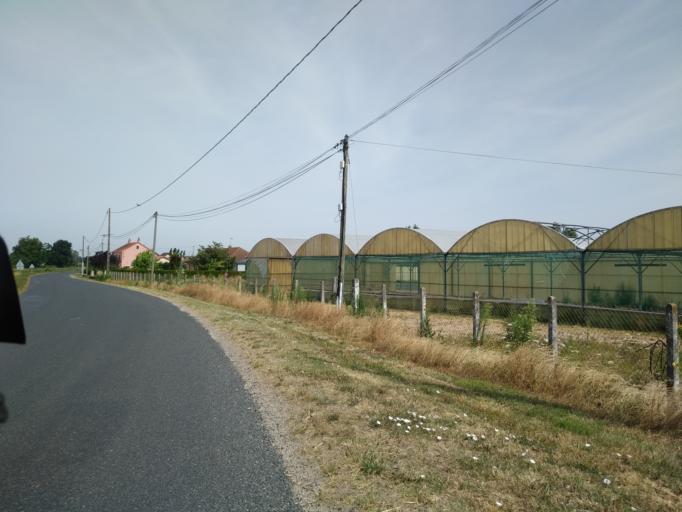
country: FR
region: Auvergne
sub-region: Departement de l'Allier
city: Molinet
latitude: 46.4534
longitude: 3.9666
